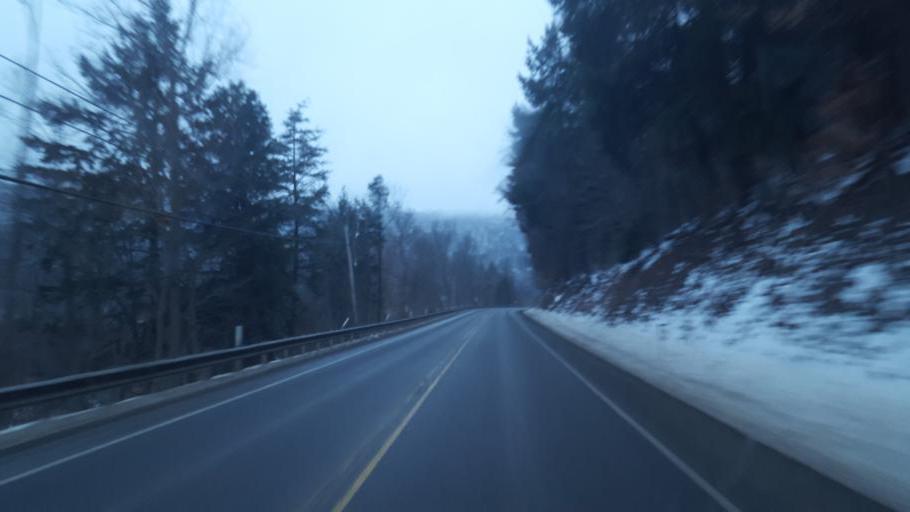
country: US
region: Pennsylvania
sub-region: Potter County
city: Coudersport
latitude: 41.7554
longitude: -78.0543
